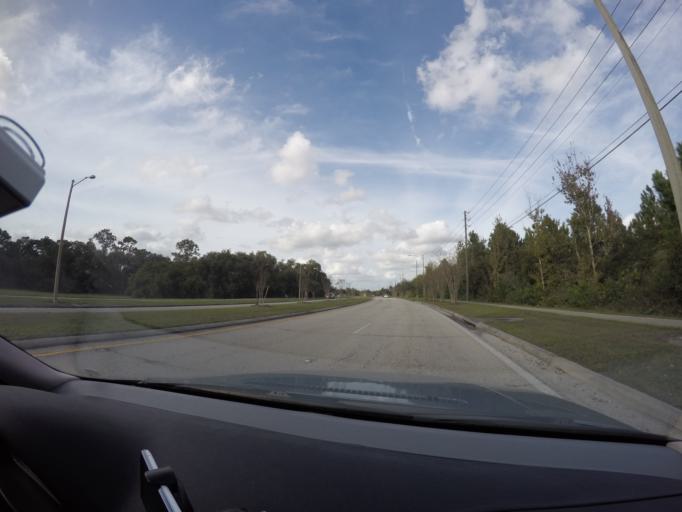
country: US
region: Florida
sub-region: Orange County
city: Wedgefield
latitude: 28.4097
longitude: -81.2090
